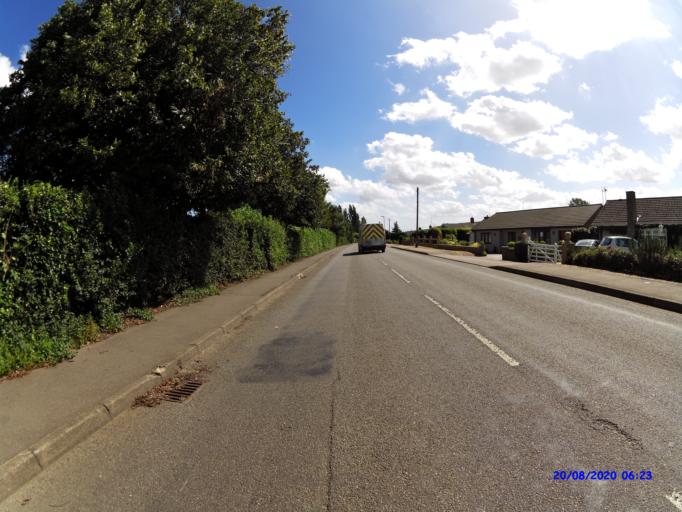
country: GB
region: England
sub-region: Cambridgeshire
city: Whittlesey
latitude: 52.5511
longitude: -0.1223
